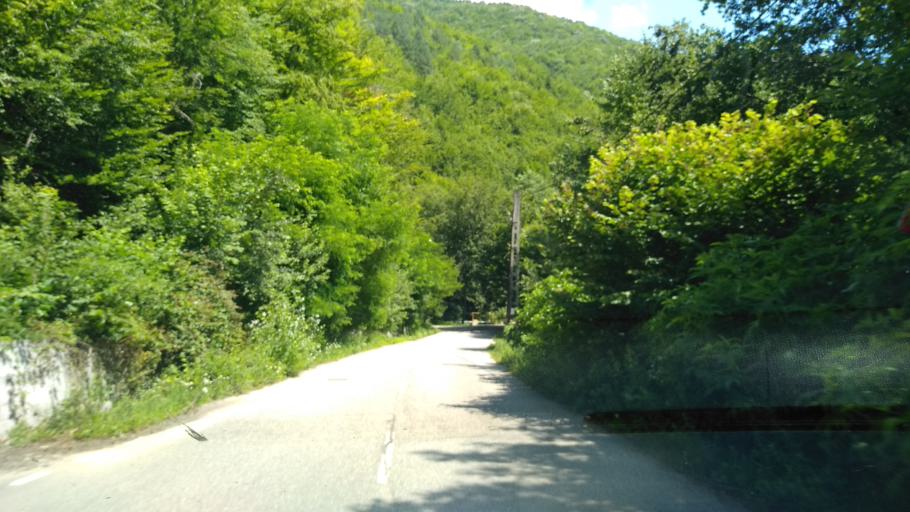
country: RO
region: Hunedoara
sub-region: Comuna Orastioara de Sus
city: Orastioara de Sus
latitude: 45.6549
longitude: 23.1868
